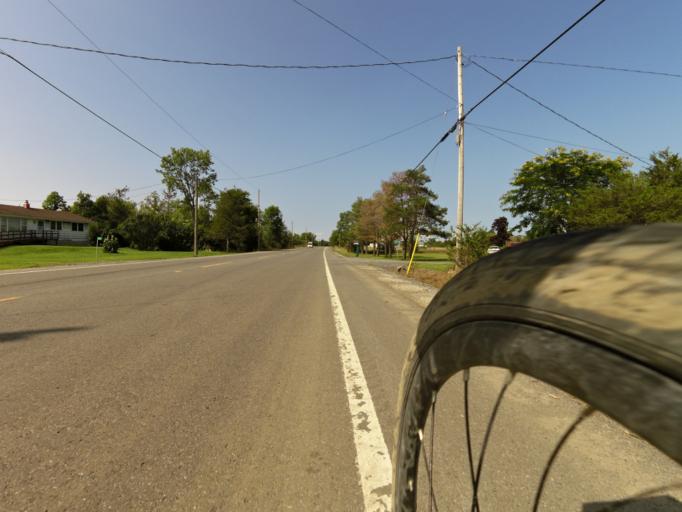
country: CA
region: Ontario
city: Skatepark
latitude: 44.2585
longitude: -76.7240
